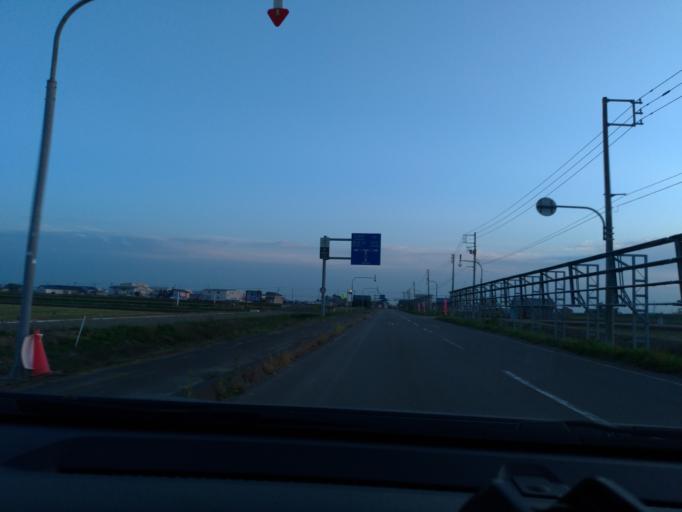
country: JP
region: Hokkaido
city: Iwamizawa
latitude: 43.3316
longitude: 141.7037
